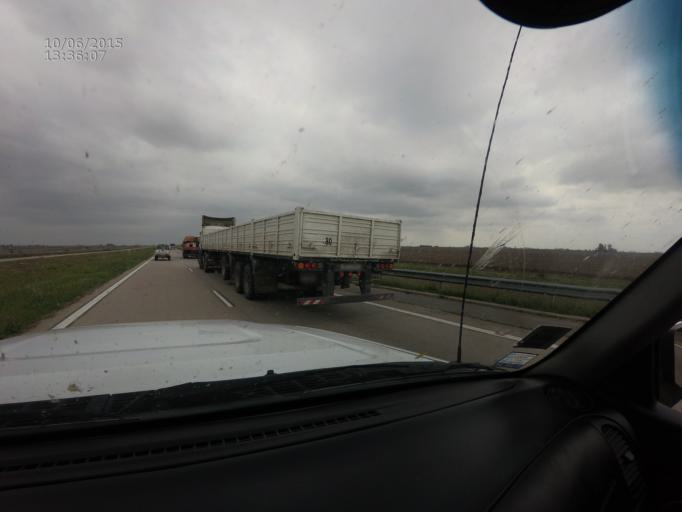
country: AR
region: Cordoba
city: Leones
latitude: -32.6135
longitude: -62.3859
